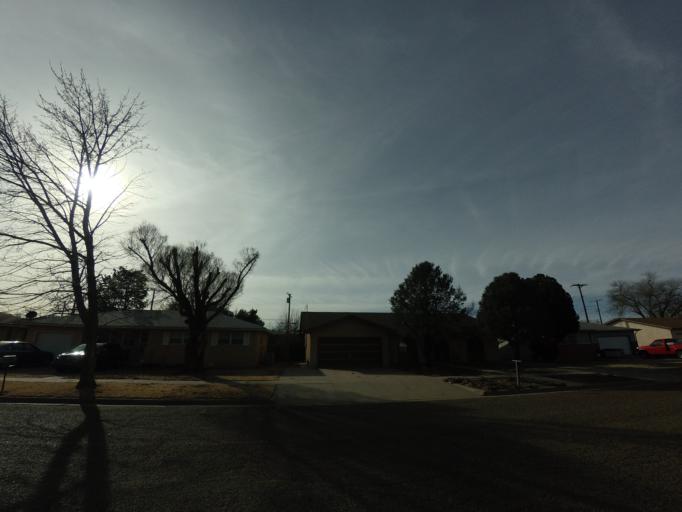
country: US
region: New Mexico
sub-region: Curry County
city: Clovis
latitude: 34.4131
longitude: -103.2165
